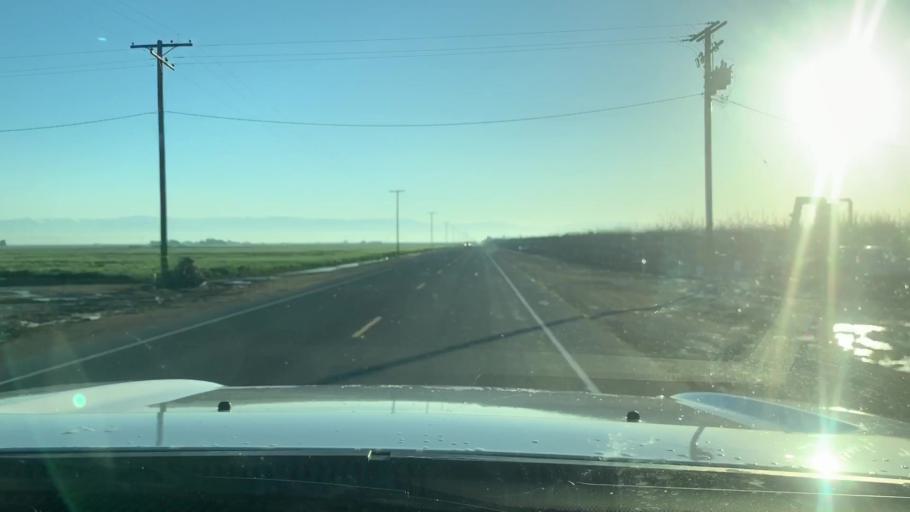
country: US
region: California
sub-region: Kings County
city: Corcoran
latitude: 36.2110
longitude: -119.5199
